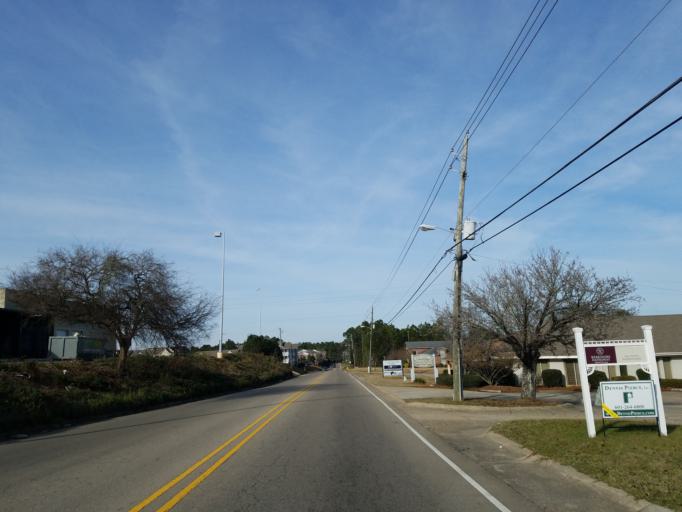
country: US
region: Mississippi
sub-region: Lamar County
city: Arnold Line
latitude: 31.3272
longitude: -89.3564
